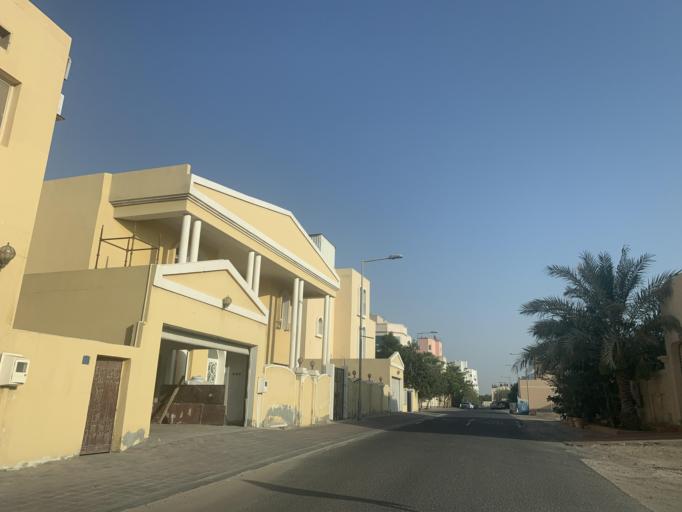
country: BH
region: Manama
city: Jidd Hafs
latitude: 26.2110
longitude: 50.5285
